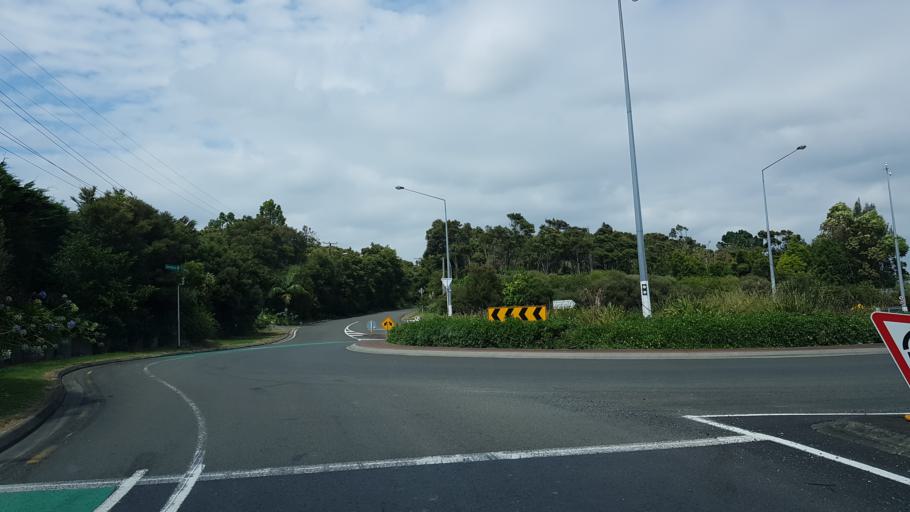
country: NZ
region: Auckland
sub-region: Auckland
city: North Shore
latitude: -36.7809
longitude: 174.6786
